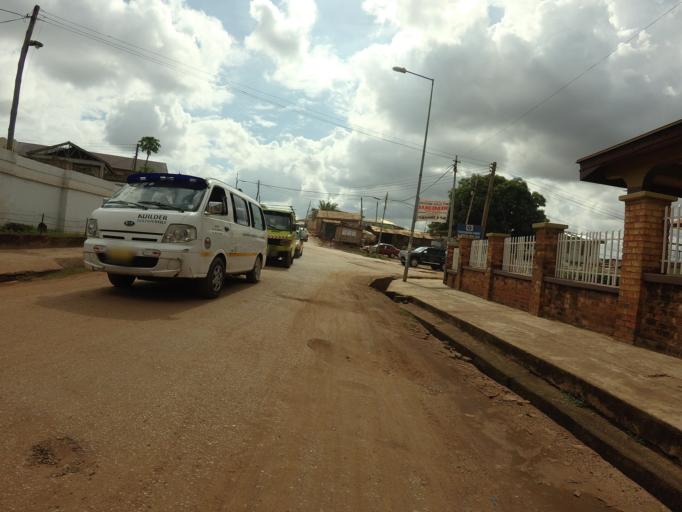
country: GH
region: Ashanti
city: Tafo
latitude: 6.7151
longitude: -1.6072
